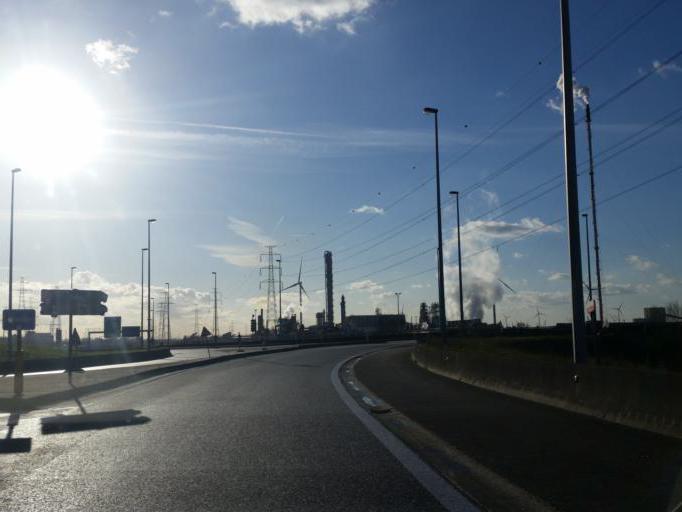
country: BE
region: Flanders
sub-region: Provincie Oost-Vlaanderen
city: Beveren
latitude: 51.2789
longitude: 4.2828
